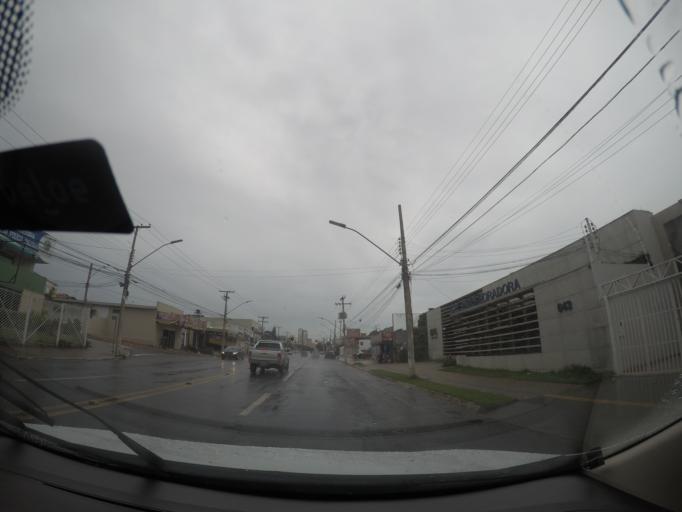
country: BR
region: Goias
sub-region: Goiania
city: Goiania
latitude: -16.6845
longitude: -49.2488
